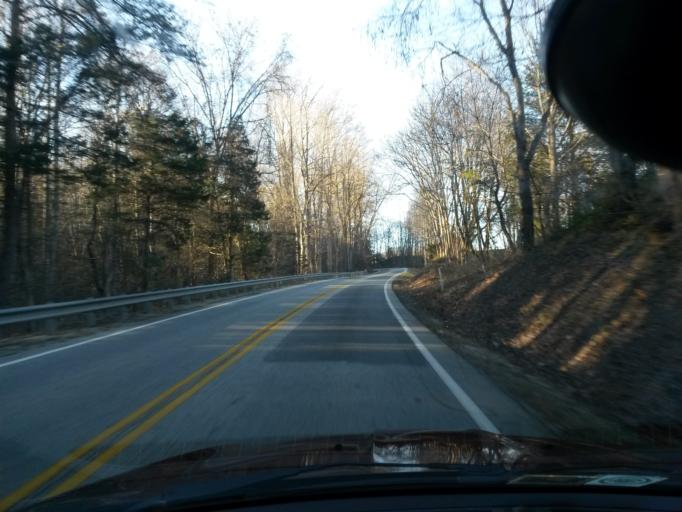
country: US
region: Virginia
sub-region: Amherst County
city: Amherst
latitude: 37.6417
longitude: -79.1210
